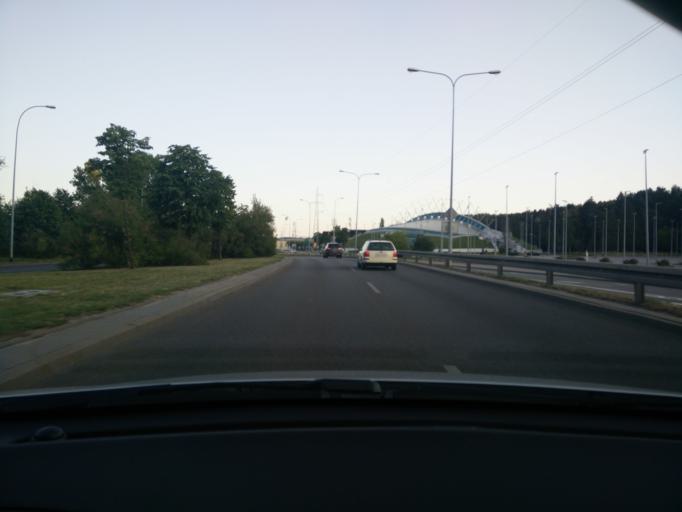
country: PL
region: Pomeranian Voivodeship
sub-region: Gdynia
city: Gdynia
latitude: 54.5017
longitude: 18.5328
